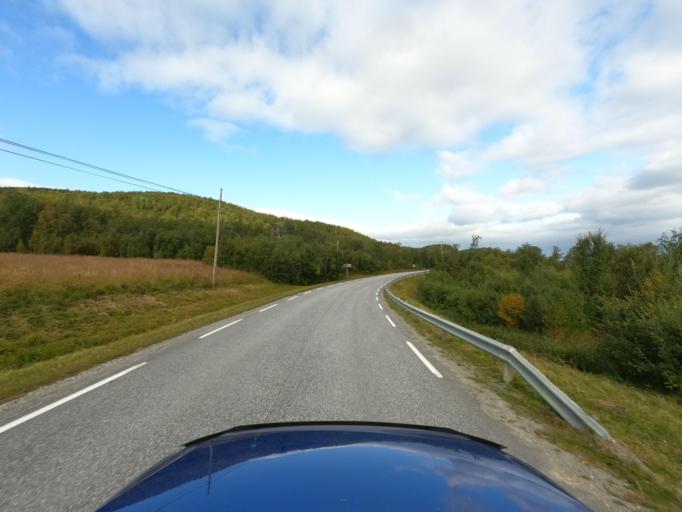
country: NO
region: Finnmark Fylke
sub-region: Porsanger
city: Lakselv
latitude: 70.2144
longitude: 24.9162
